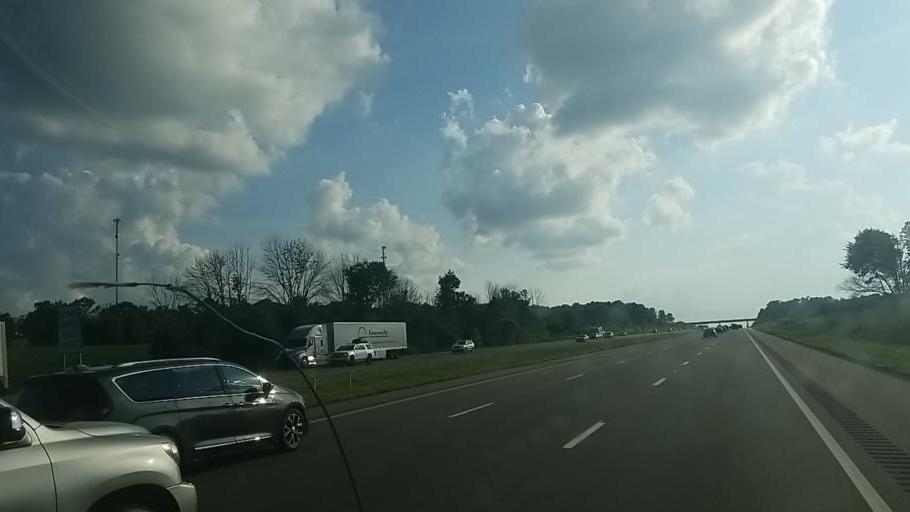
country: US
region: Ohio
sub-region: Ashland County
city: Ashland
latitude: 40.8395
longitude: -82.2908
